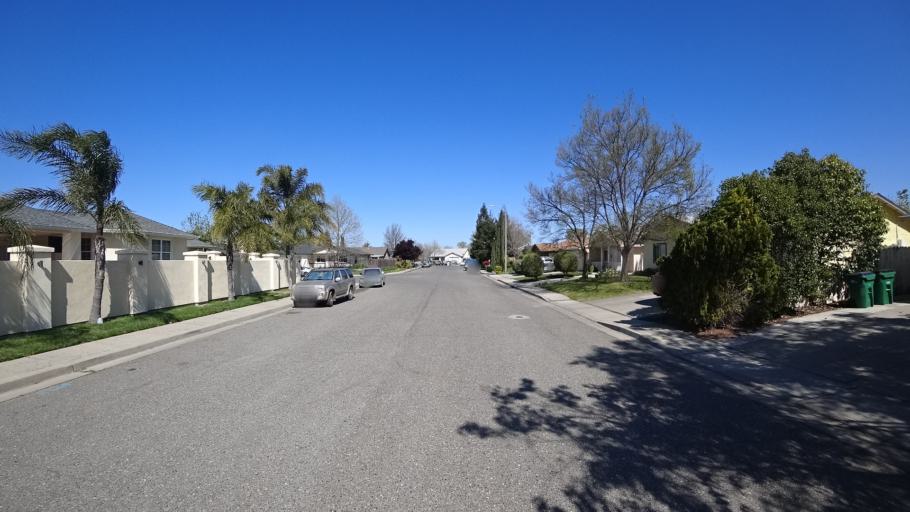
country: US
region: California
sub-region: Glenn County
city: Hamilton City
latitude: 39.7463
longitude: -122.0061
